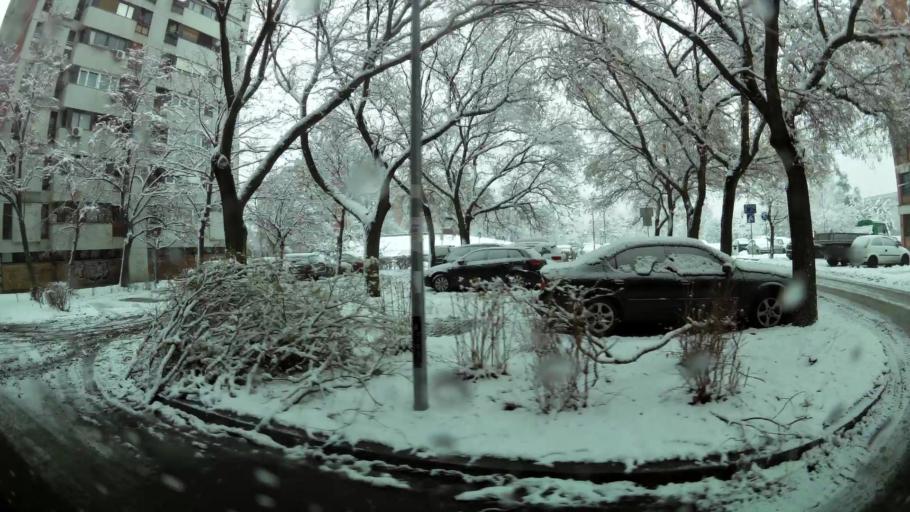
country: RS
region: Central Serbia
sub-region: Belgrade
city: Novi Beograd
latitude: 44.8005
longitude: 20.3899
